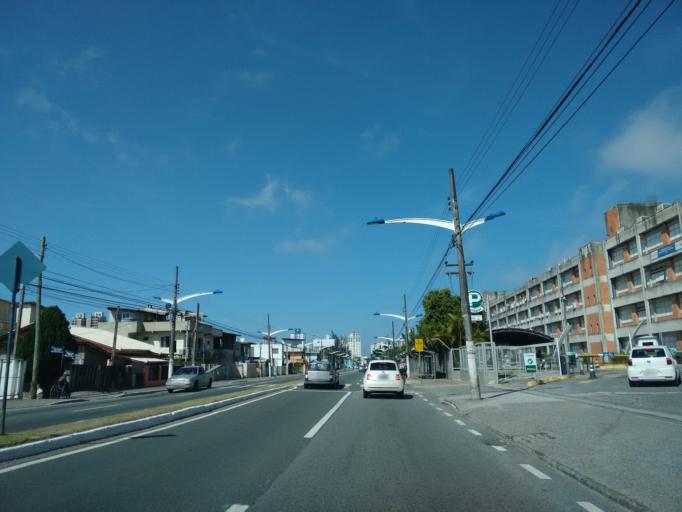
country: BR
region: Santa Catarina
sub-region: Itajai
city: Itajai
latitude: -26.9183
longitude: -48.6685
